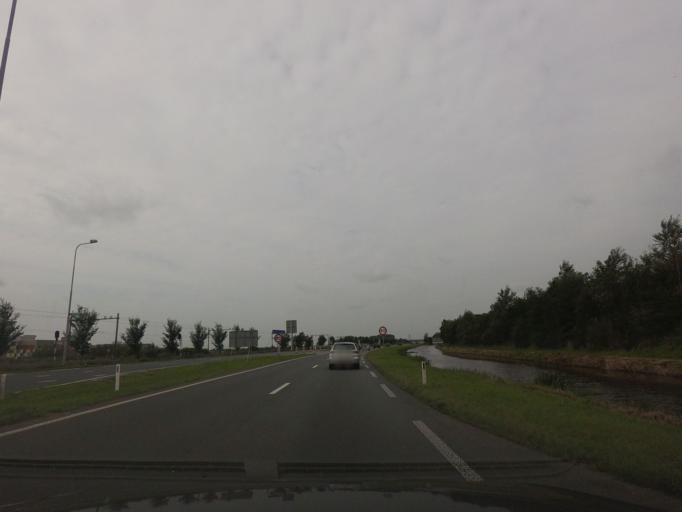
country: NL
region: North Holland
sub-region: Gemeente Uitgeest
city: Uitgeest
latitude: 52.4964
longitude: 4.7515
